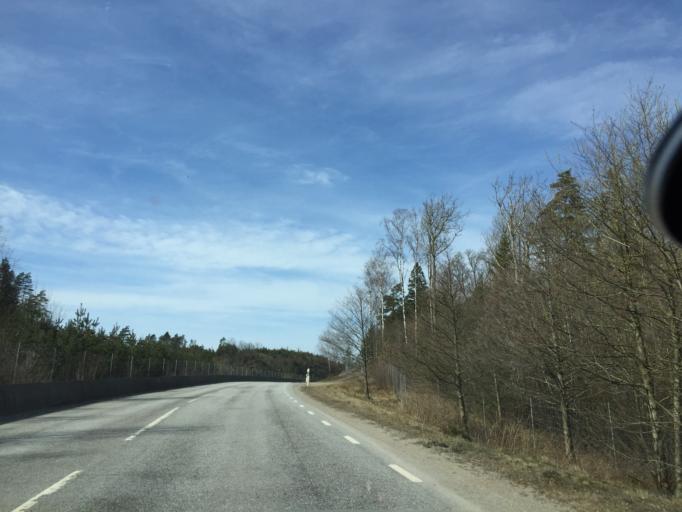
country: SE
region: Vaestra Goetaland
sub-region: Uddevalla Kommun
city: Uddevalla
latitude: 58.3646
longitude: 11.8016
